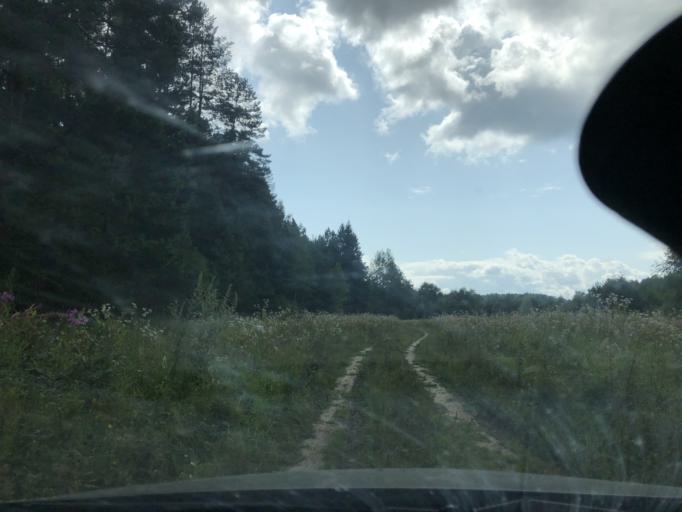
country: RU
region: Kaluga
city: Yukhnov
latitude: 54.7289
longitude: 35.1161
